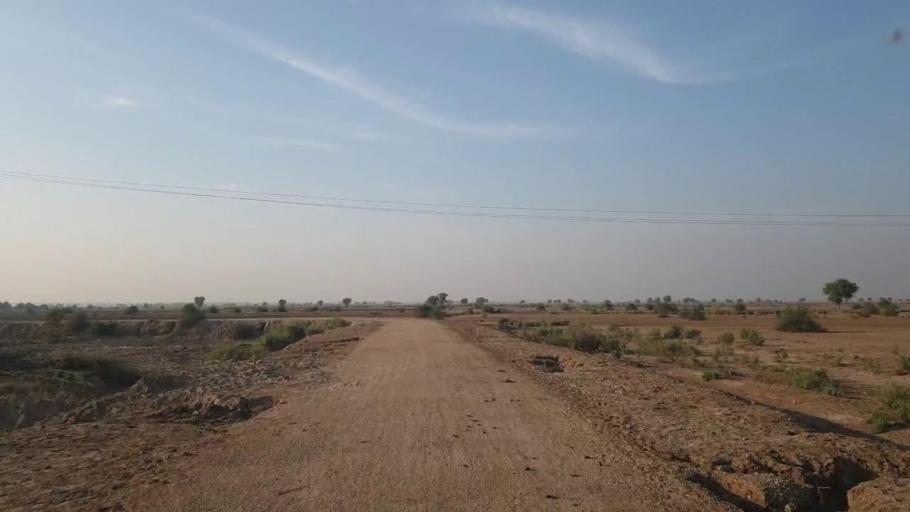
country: PK
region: Sindh
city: Sann
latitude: 25.9477
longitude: 68.1778
